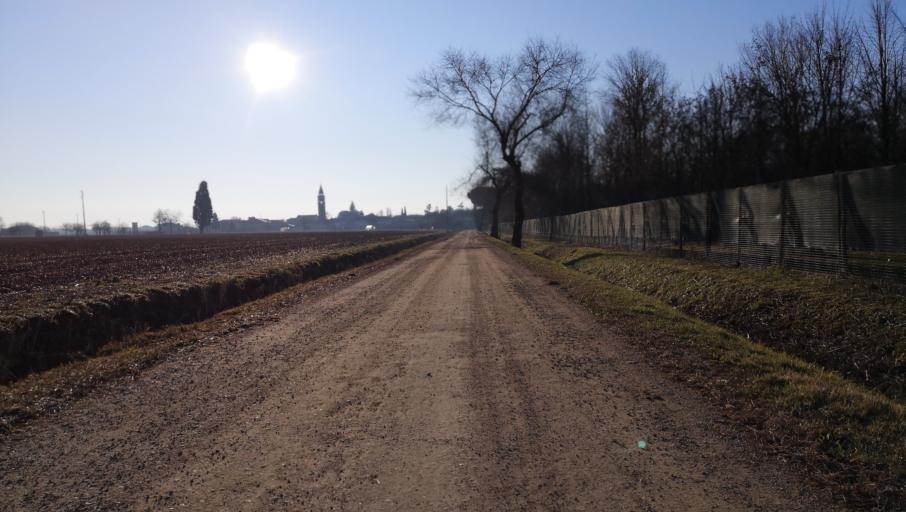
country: IT
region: Friuli Venezia Giulia
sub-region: Provincia di Udine
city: Lauzacco
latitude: 45.9693
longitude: 13.2945
